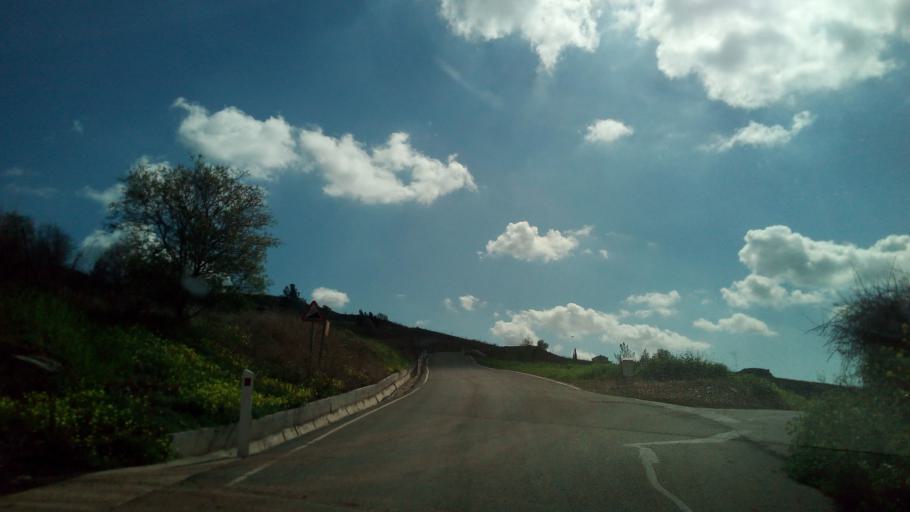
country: CY
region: Pafos
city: Mesogi
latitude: 34.7743
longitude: 32.5836
